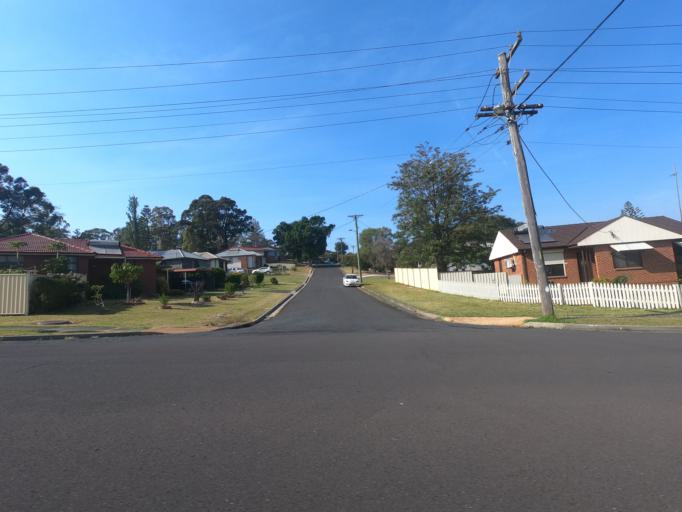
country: AU
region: New South Wales
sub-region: Wollongong
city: Berkeley
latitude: -34.4755
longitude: 150.8434
